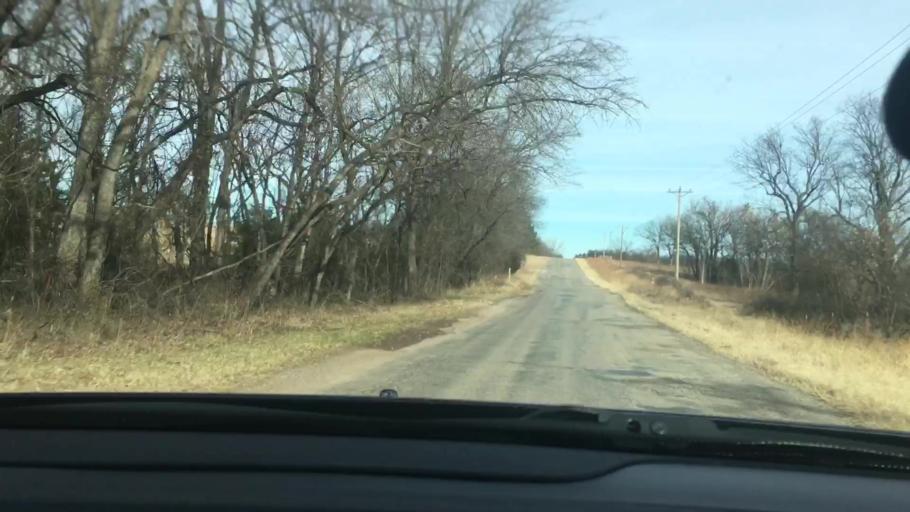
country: US
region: Oklahoma
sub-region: Garvin County
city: Wynnewood
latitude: 34.6412
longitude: -97.2475
